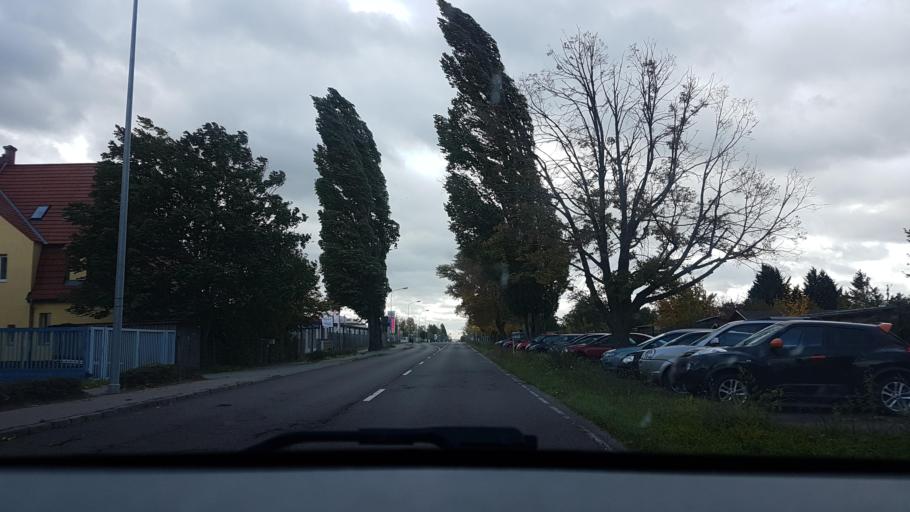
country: DE
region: Saxony-Anhalt
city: Bernburg
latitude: 51.7811
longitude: 11.7457
